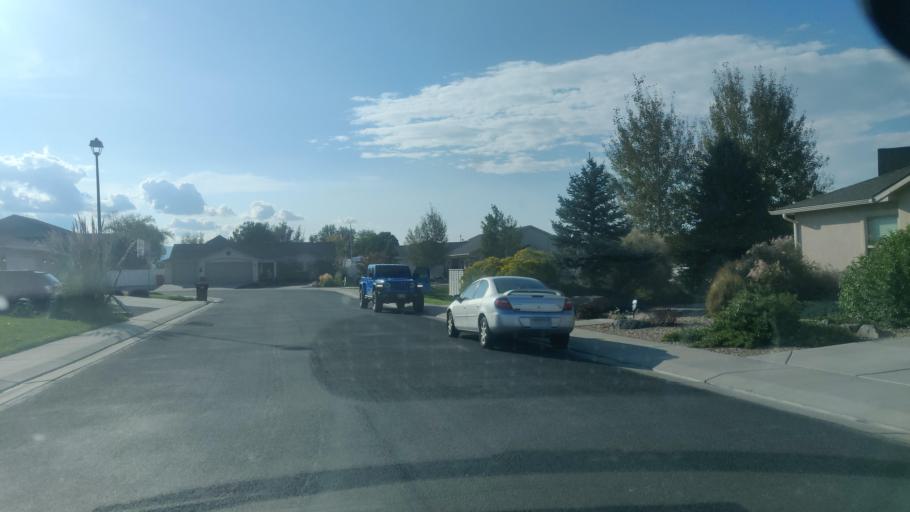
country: US
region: Colorado
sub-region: Mesa County
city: Fruitvale
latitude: 39.0335
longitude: -108.4974
